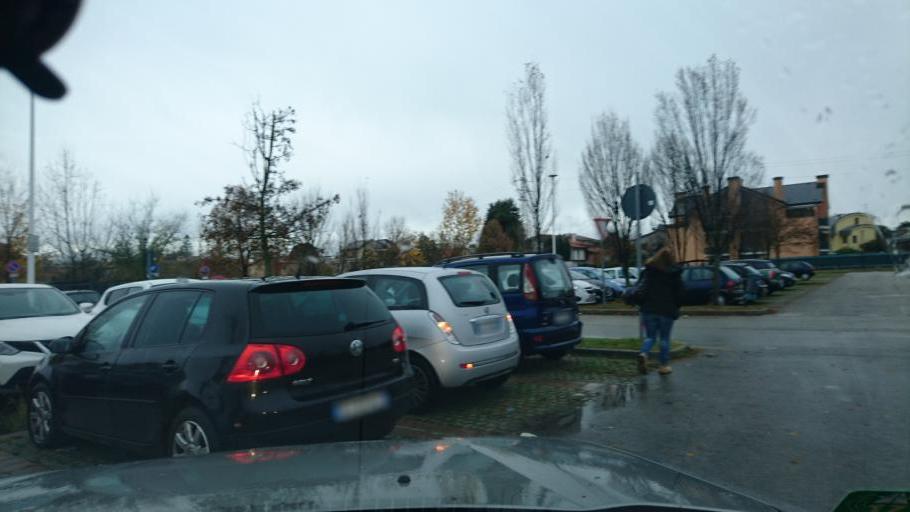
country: IT
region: Veneto
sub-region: Provincia di Treviso
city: Castelfranco Veneto
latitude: 45.6678
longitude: 11.9371
